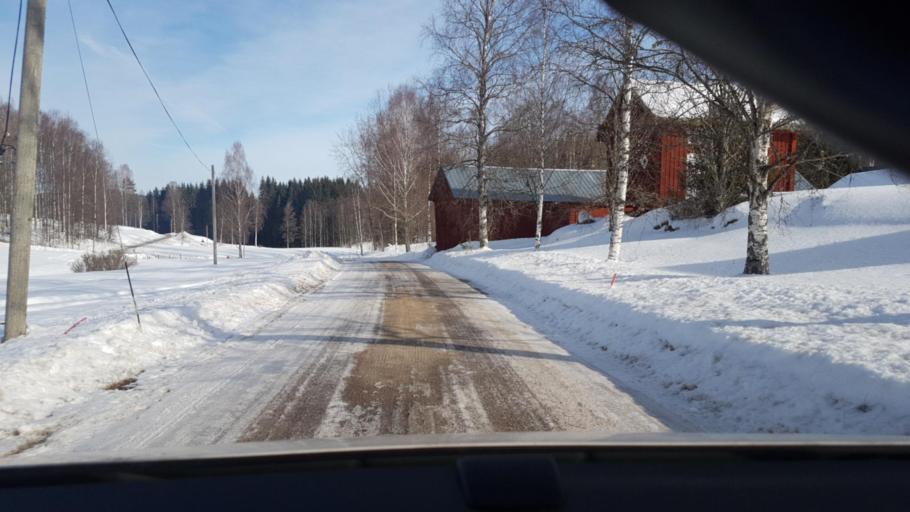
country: NO
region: Ostfold
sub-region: Romskog
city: Romskog
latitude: 59.8157
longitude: 11.9962
